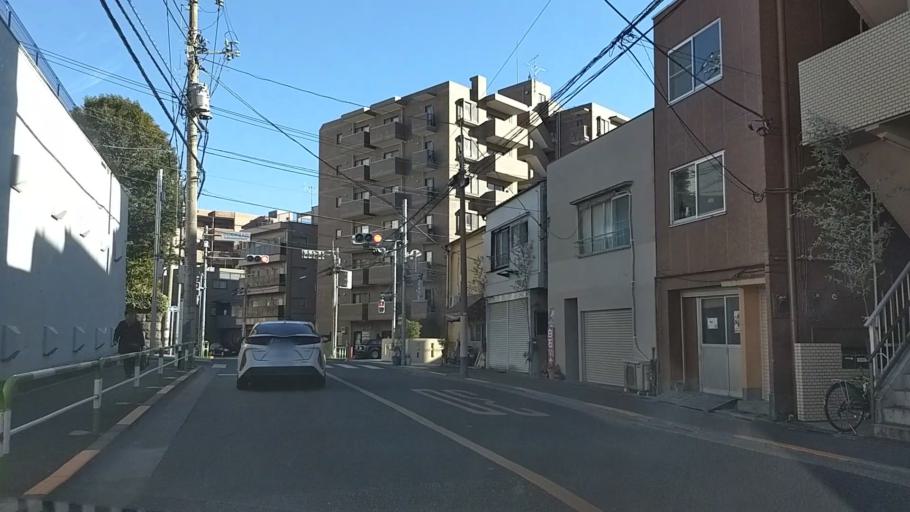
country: JP
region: Tokyo
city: Tokyo
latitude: 35.7103
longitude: 139.7346
